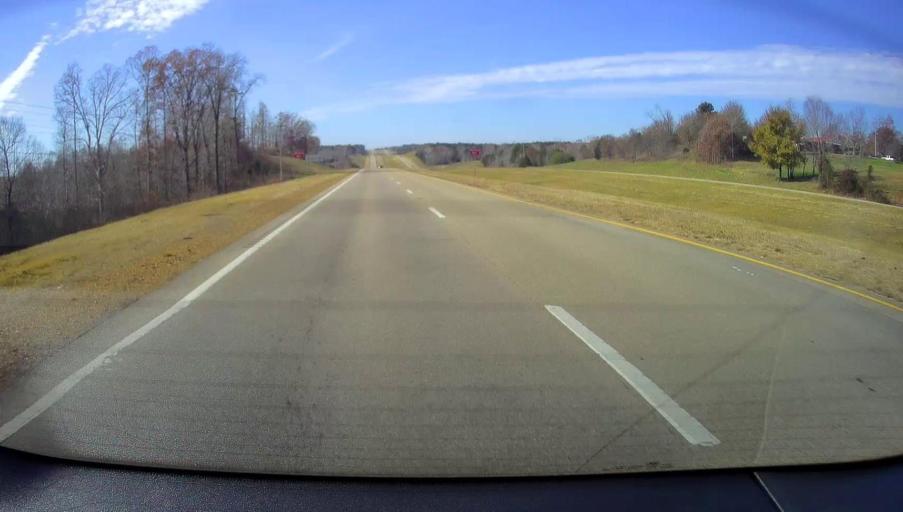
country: US
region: Mississippi
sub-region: Tippah County
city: Ripley
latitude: 34.9550
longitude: -88.9627
